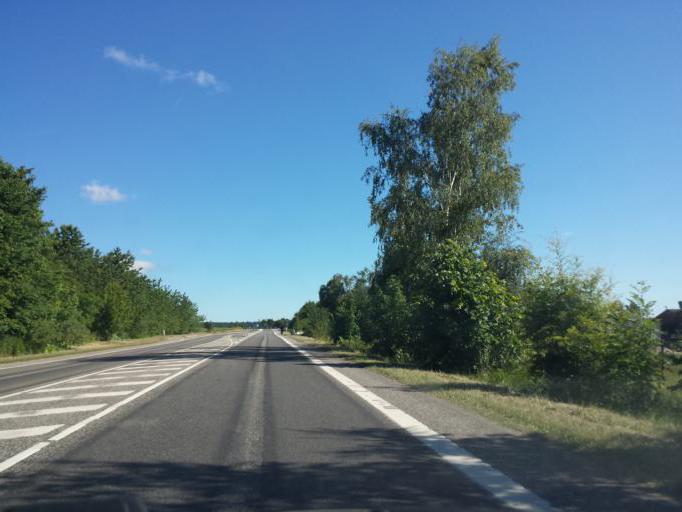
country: DK
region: Capital Region
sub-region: Egedal Kommune
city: Smorumnedre
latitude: 55.7615
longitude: 12.2937
